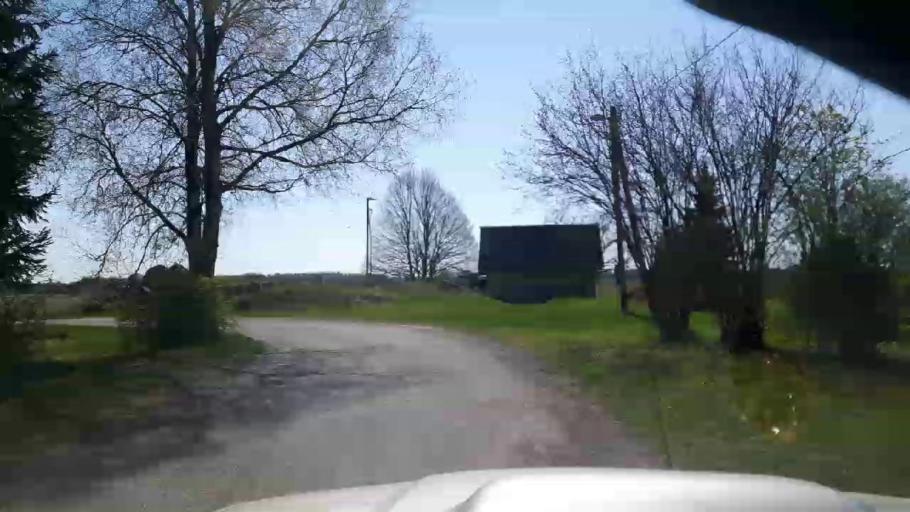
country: EE
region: Paernumaa
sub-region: Tootsi vald
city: Tootsi
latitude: 58.4762
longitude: 24.7979
